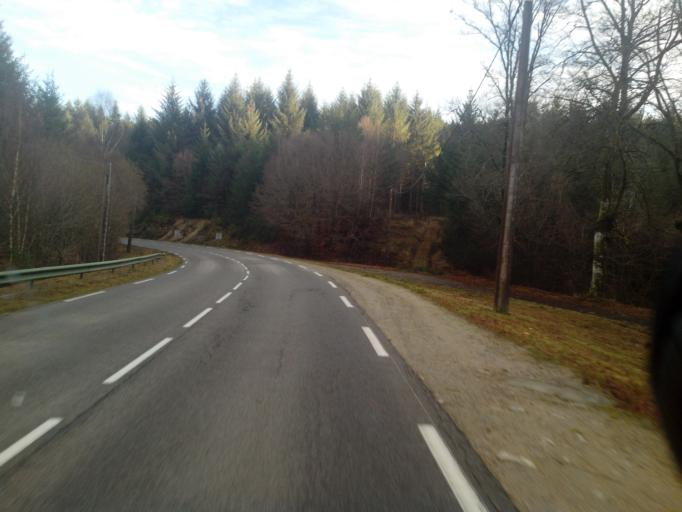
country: FR
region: Limousin
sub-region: Departement de la Correze
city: Bugeat
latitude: 45.6362
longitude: 1.8314
